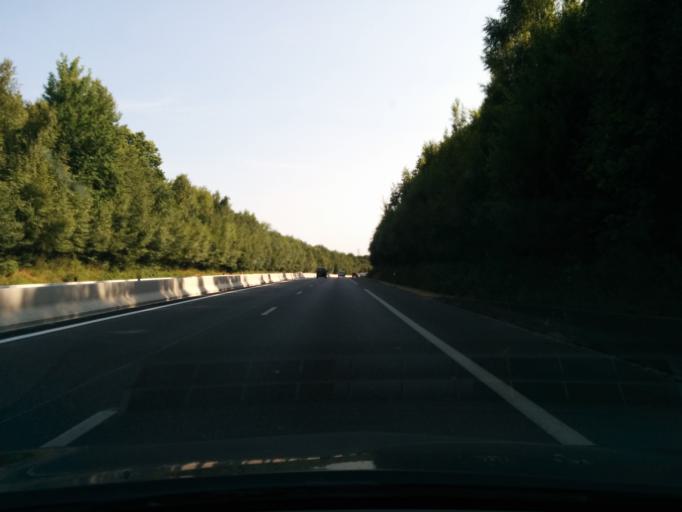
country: FR
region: Limousin
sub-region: Departement de la Haute-Vienne
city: Le Palais-sur-Vienne
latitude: 45.8661
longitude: 1.2875
